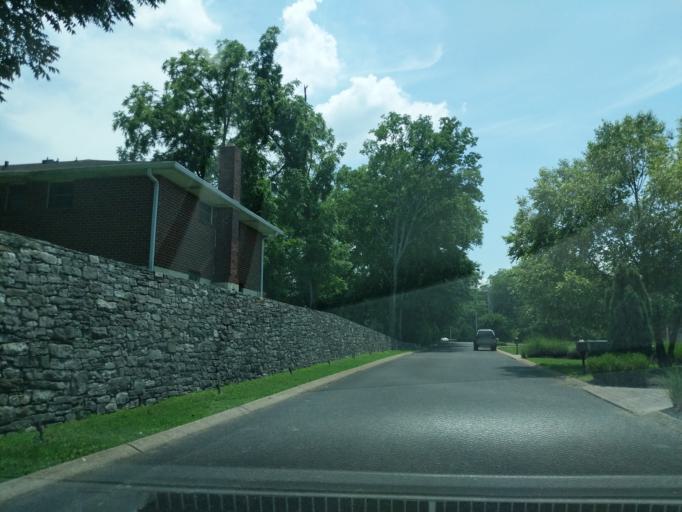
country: US
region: Tennessee
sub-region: Davidson County
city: Lakewood
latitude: 36.2449
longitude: -86.6297
